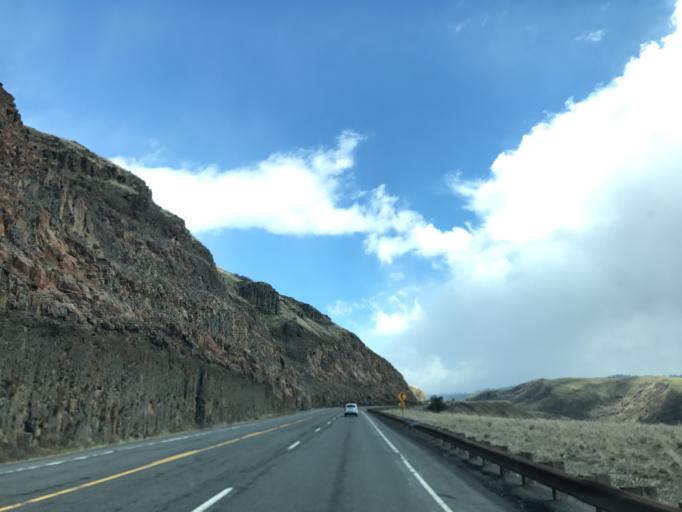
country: US
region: Idaho
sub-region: Idaho County
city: Grangeville
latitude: 45.8190
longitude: -116.2728
